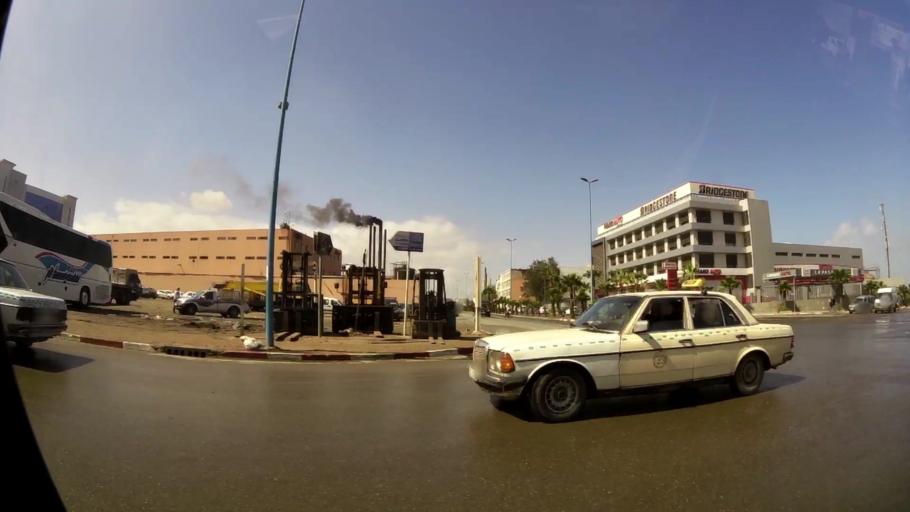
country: MA
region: Grand Casablanca
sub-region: Mediouna
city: Tit Mellil
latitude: 33.6239
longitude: -7.5066
